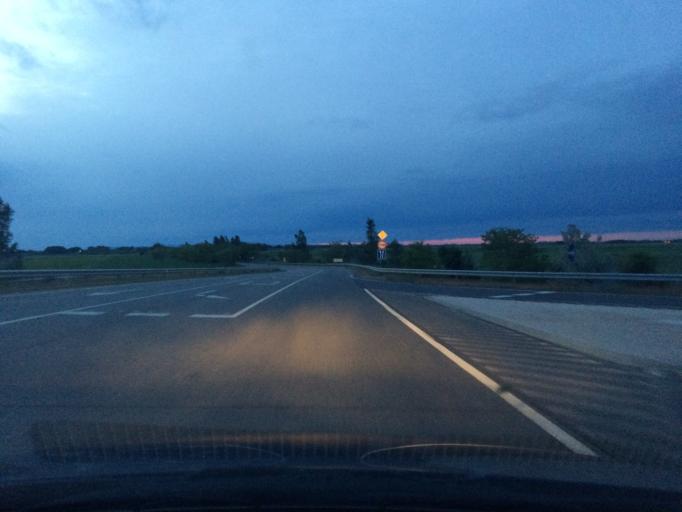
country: HU
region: Hajdu-Bihar
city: Hajdunanas
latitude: 47.8837
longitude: 21.4141
